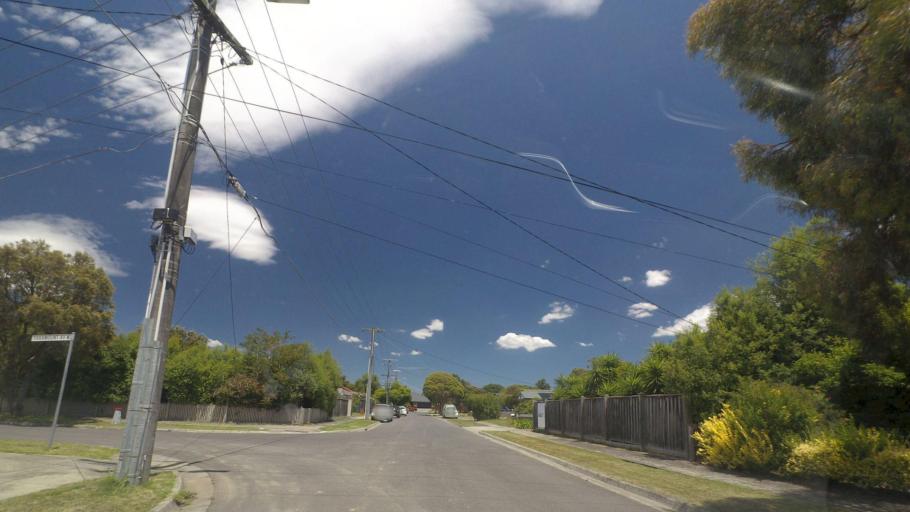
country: AU
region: Victoria
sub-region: Maroondah
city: Kilsyth South
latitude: -37.8126
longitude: 145.3135
